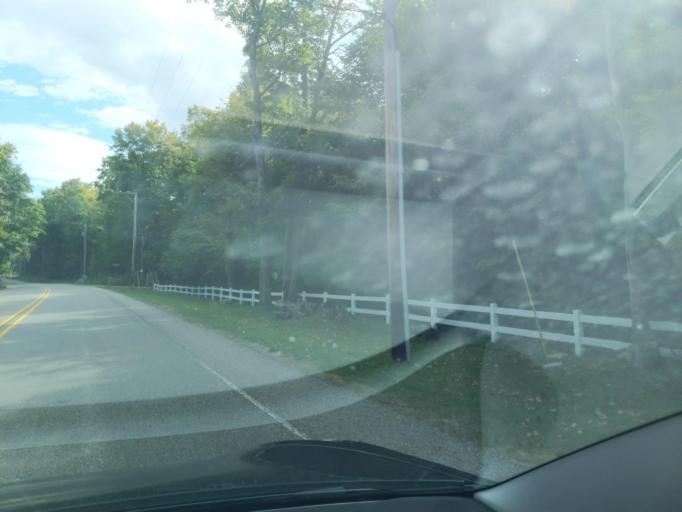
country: US
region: Michigan
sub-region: Antrim County
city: Bellaire
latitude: 44.9329
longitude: -85.2872
